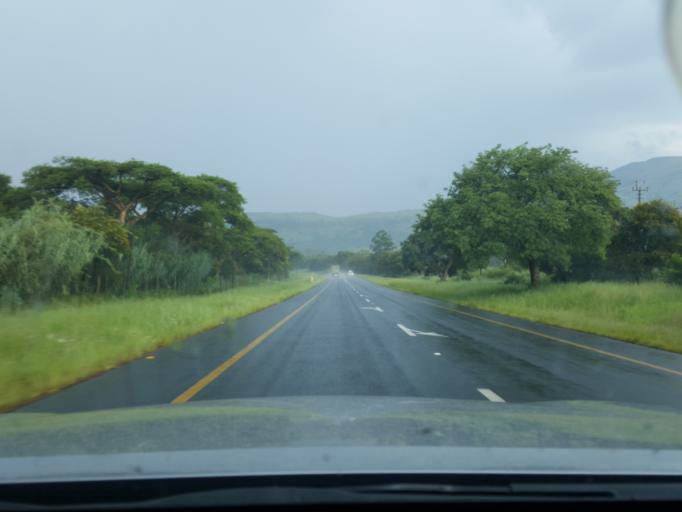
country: ZA
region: Mpumalanga
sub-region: Nkangala District Municipality
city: Belfast
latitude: -25.6117
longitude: 30.4238
